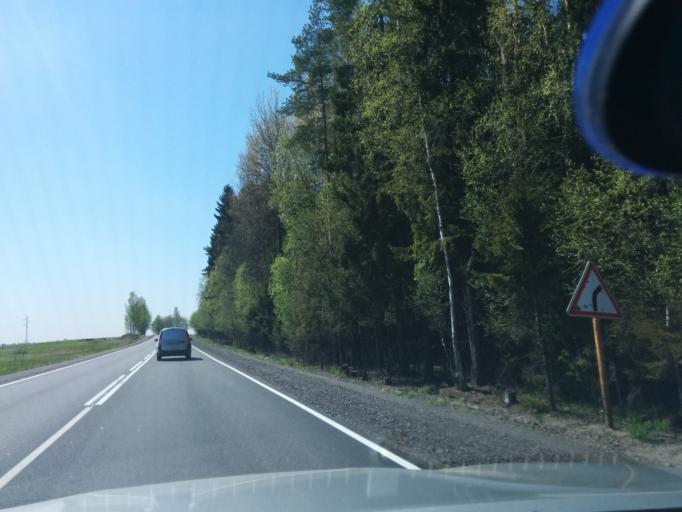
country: RU
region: Leningrad
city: Verkhniye Osel'ki
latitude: 60.1910
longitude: 30.4131
